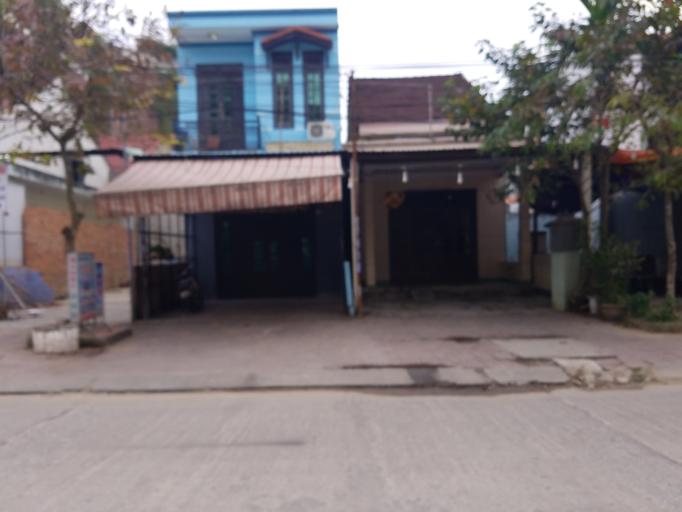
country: VN
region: Quang Nam
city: Hoi An
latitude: 15.8769
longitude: 108.3221
